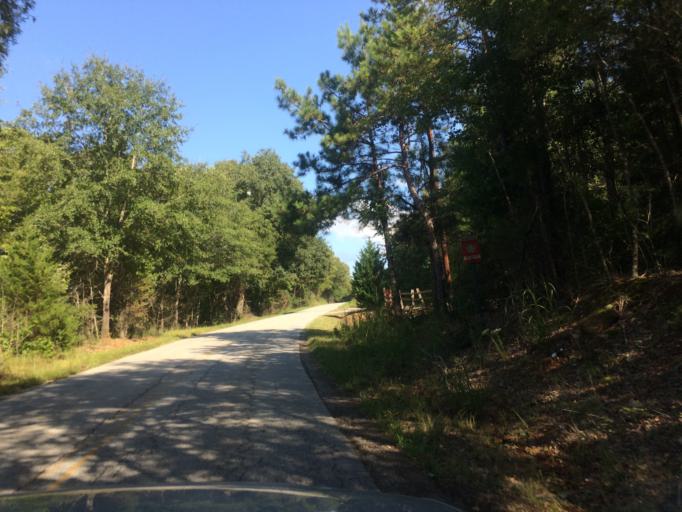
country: US
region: South Carolina
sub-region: Greenwood County
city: Ware Shoals
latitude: 34.4348
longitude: -82.2629
